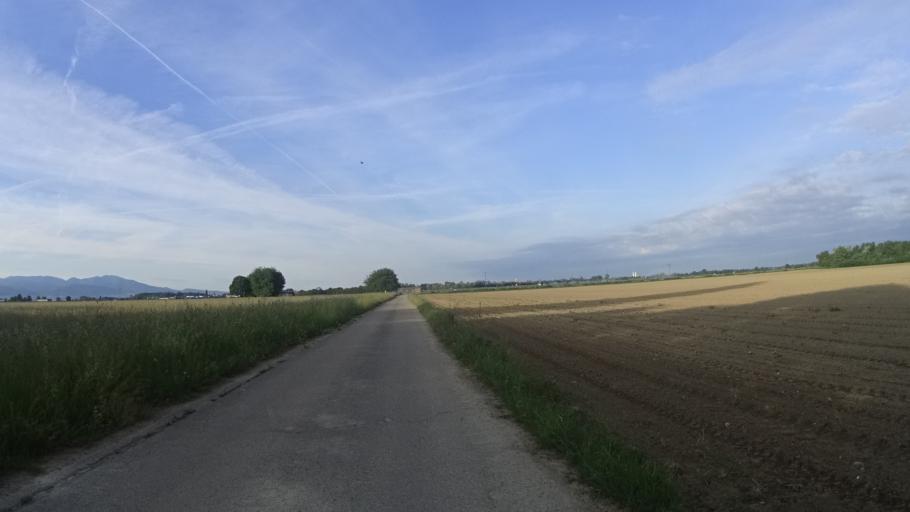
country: DE
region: Baden-Wuerttemberg
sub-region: Freiburg Region
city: Hartheim
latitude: 47.9548
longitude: 7.6498
